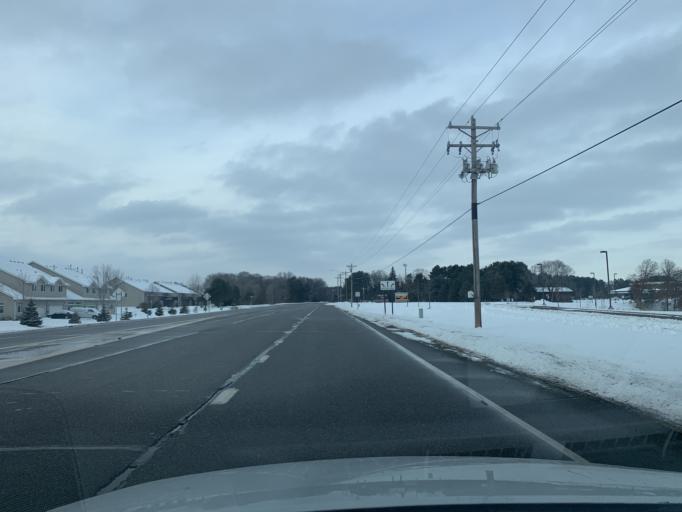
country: US
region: Minnesota
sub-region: Anoka County
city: Anoka
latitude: 45.2326
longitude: -93.4024
